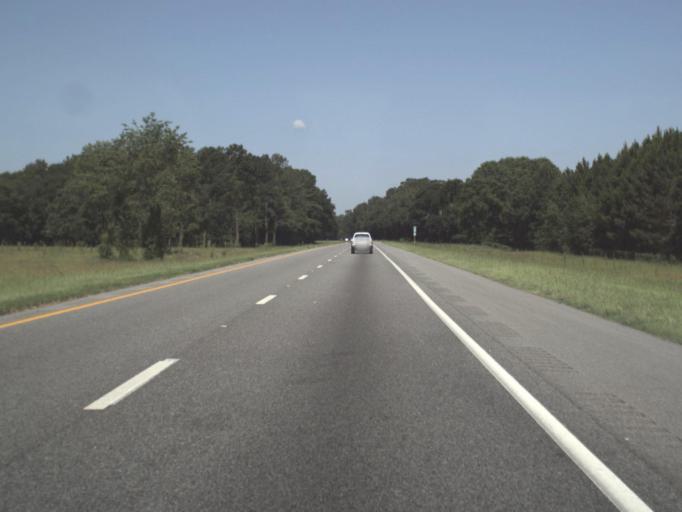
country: US
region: Florida
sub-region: Suwannee County
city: Live Oak
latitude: 30.3527
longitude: -83.0352
